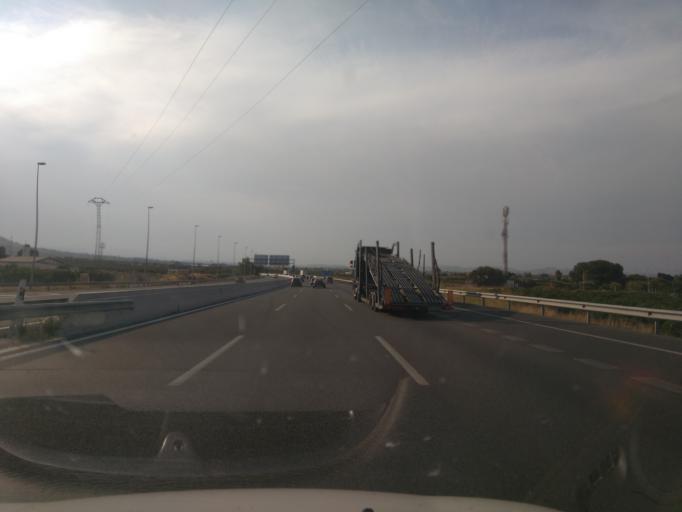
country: ES
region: Valencia
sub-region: Provincia de Valencia
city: Torrent
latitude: 39.4192
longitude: -0.5121
